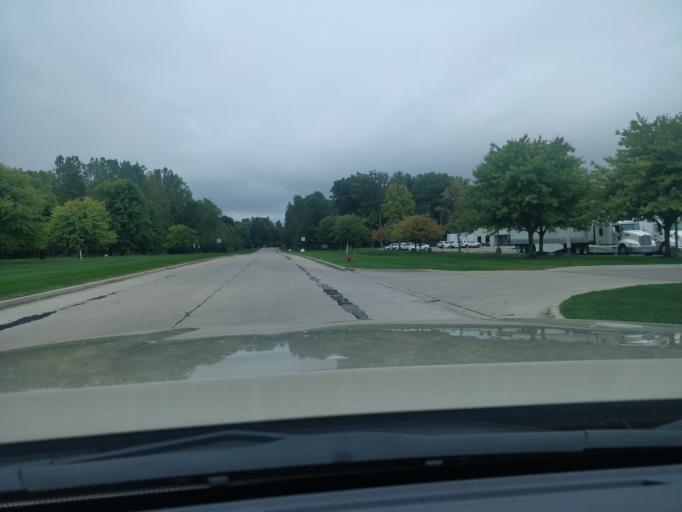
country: US
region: Michigan
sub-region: Wayne County
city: Romulus
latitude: 42.1744
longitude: -83.3920
